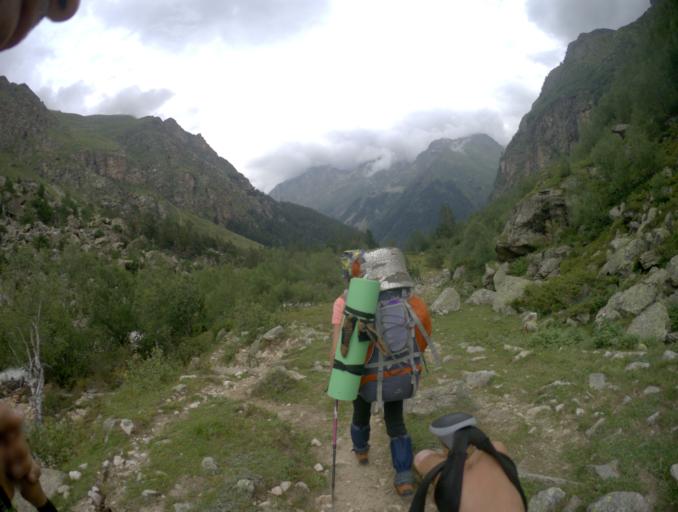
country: RU
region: Karachayevo-Cherkesiya
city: Uchkulan
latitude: 43.2686
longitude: 42.1492
